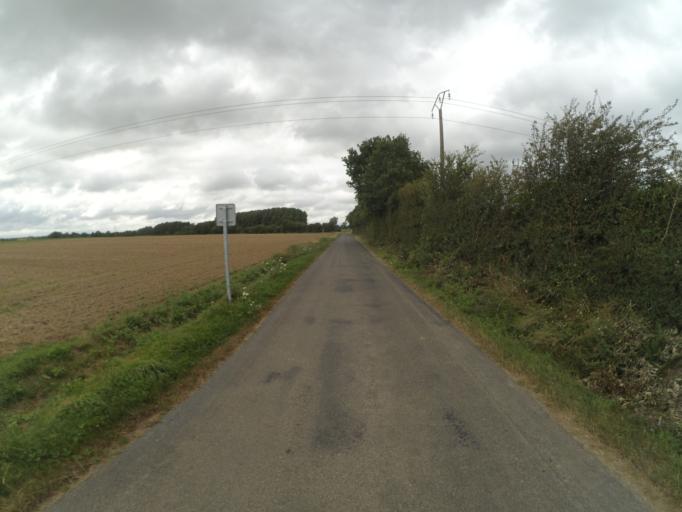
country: FR
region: Pays de la Loire
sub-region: Departement de la Vendee
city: Saint-Philbert-de-Bouaine
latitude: 46.9978
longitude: -1.5256
